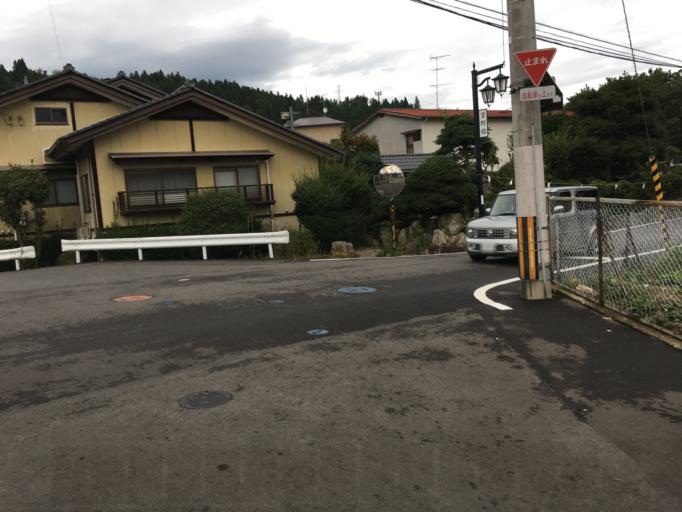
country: JP
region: Fukushima
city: Fukushima-shi
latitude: 37.8368
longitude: 140.4488
